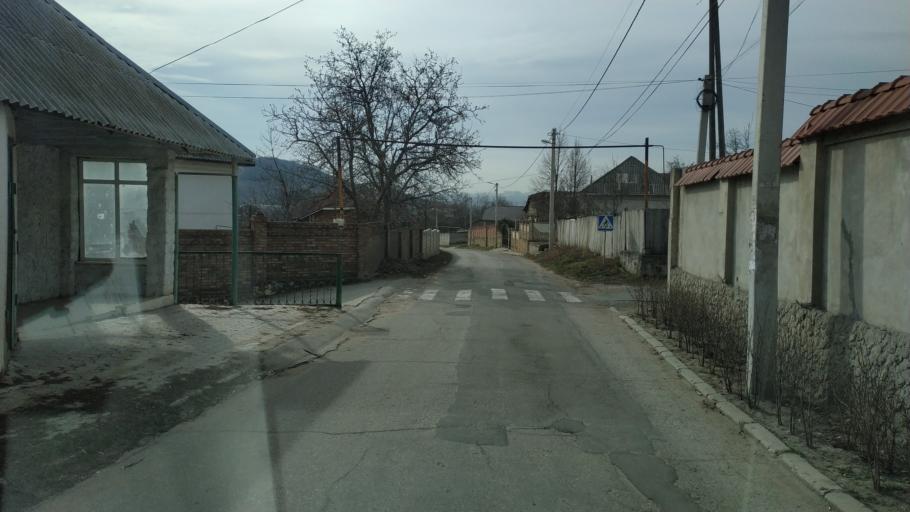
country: MD
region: Chisinau
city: Vatra
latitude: 47.0912
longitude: 28.7687
